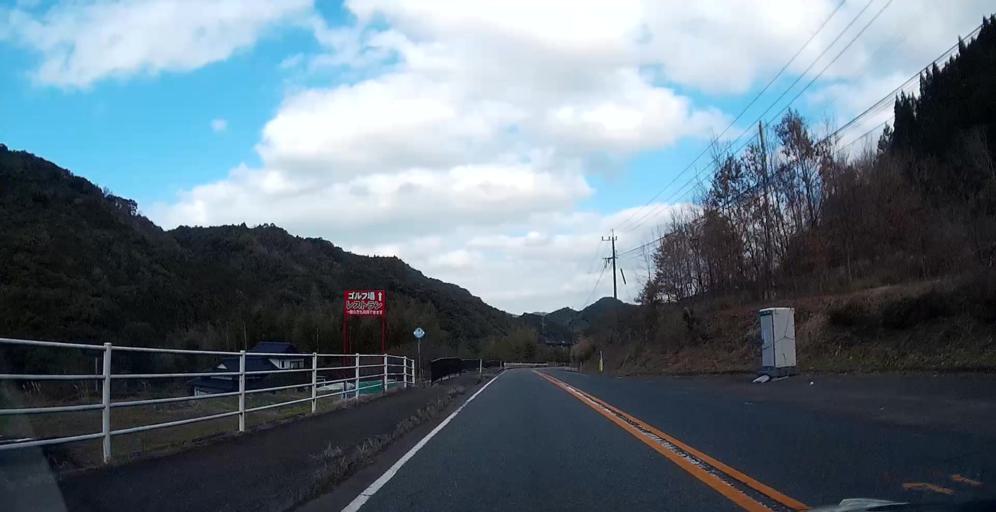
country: JP
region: Kumamoto
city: Yatsushiro
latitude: 32.3799
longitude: 130.5370
